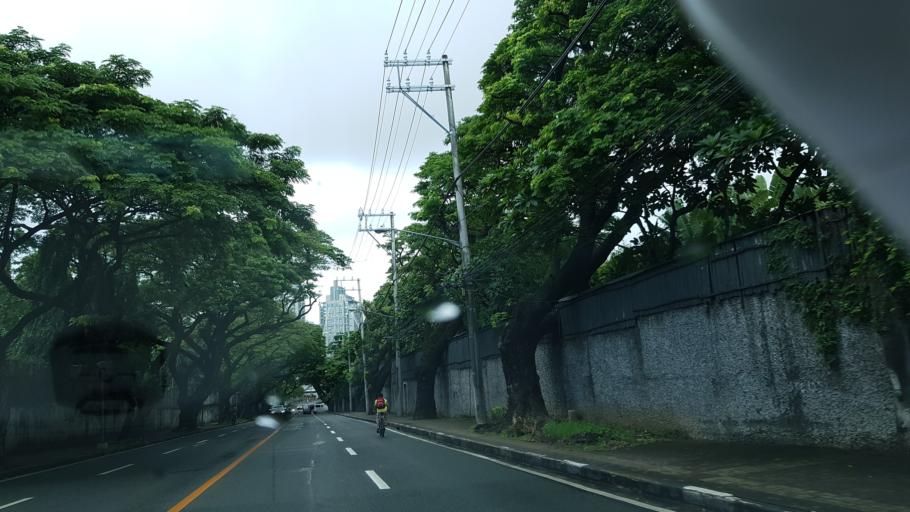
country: PH
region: Metro Manila
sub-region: Makati City
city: Makati City
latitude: 14.5485
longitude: 121.0324
